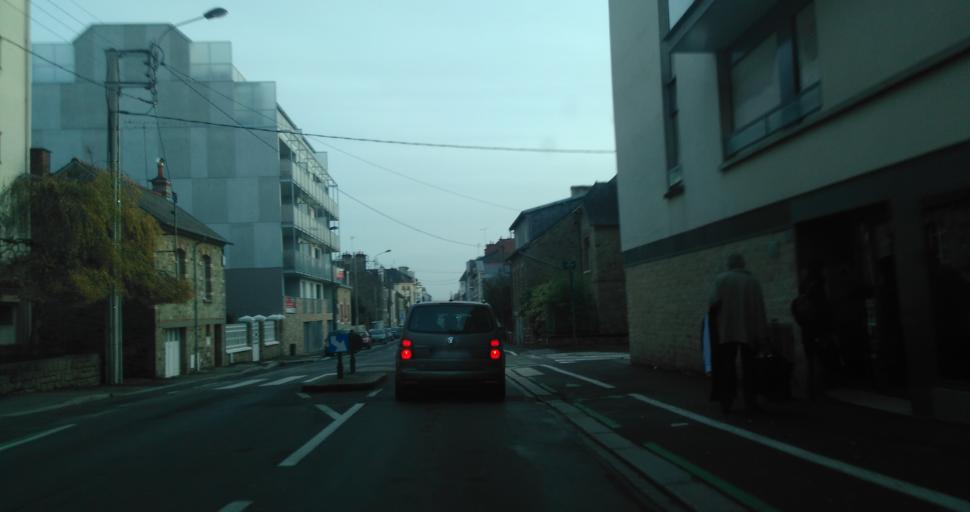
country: FR
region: Brittany
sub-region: Departement d'Ille-et-Vilaine
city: Rennes
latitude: 48.1206
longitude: -1.6618
